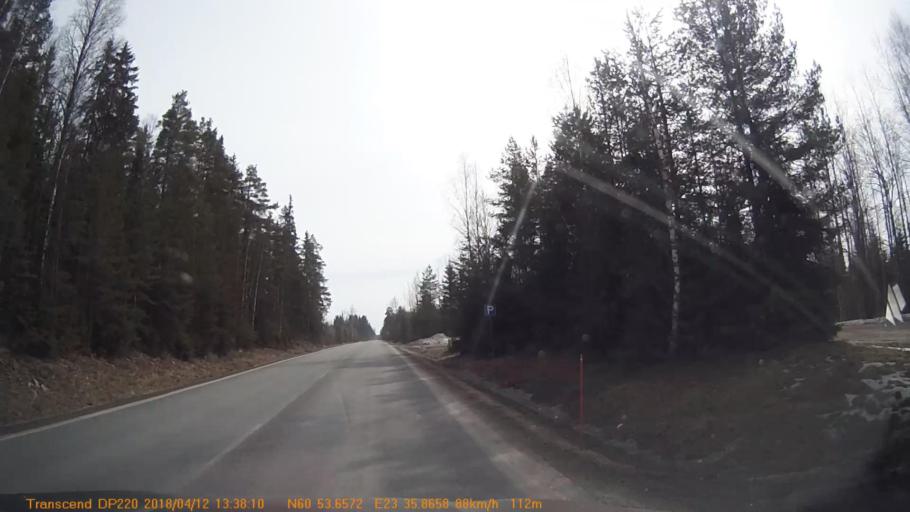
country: FI
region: Haeme
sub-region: Forssa
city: Forssa
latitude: 60.8939
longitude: 23.5979
